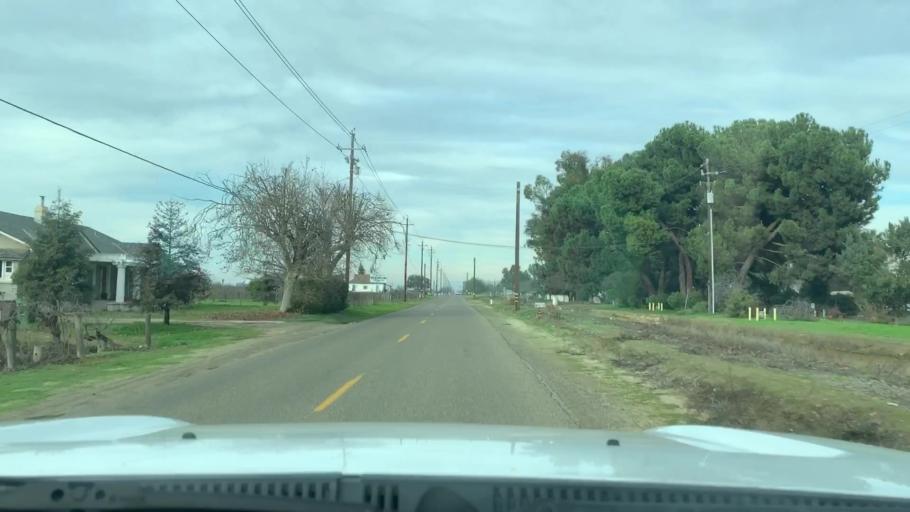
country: US
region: California
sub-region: Fresno County
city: Selma
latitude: 36.5806
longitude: -119.5749
